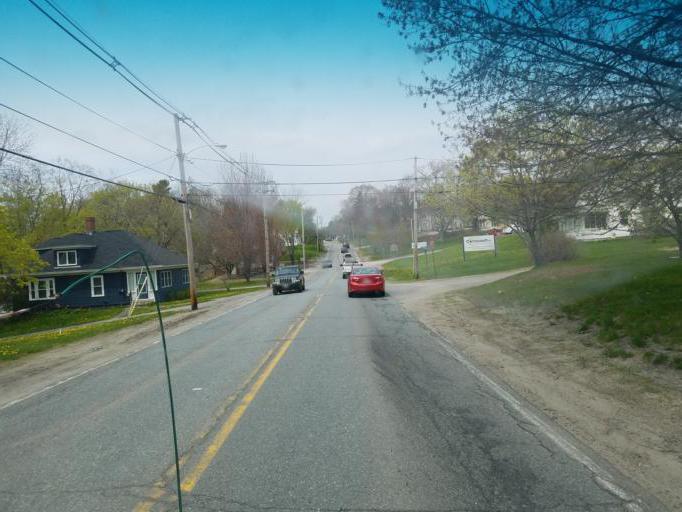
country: US
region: Maine
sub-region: Hancock County
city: Ellsworth
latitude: 44.5448
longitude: -68.4215
